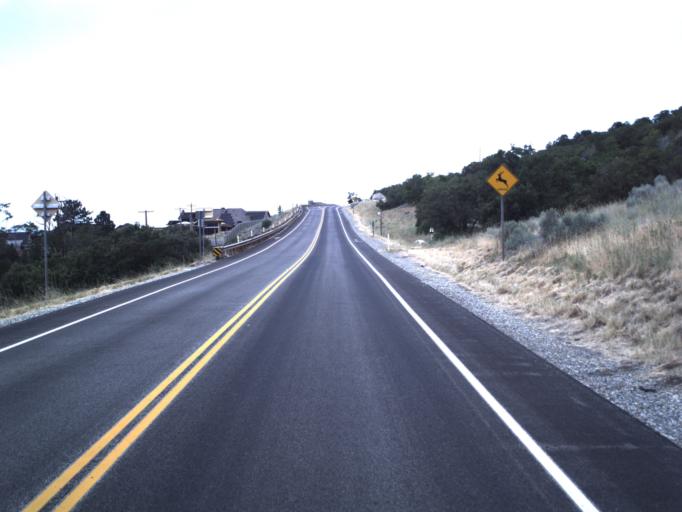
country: US
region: Utah
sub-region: Salt Lake County
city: Granite
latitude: 40.5779
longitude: -111.7897
